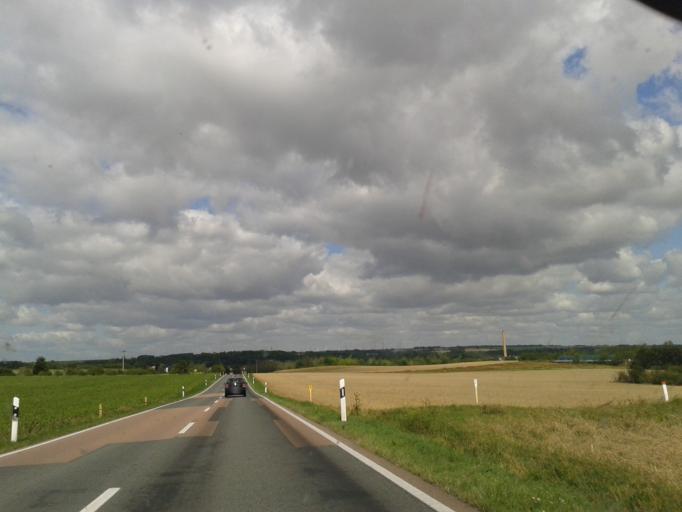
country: DE
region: Saxony-Anhalt
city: Salzmunde
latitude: 51.5226
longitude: 11.8445
